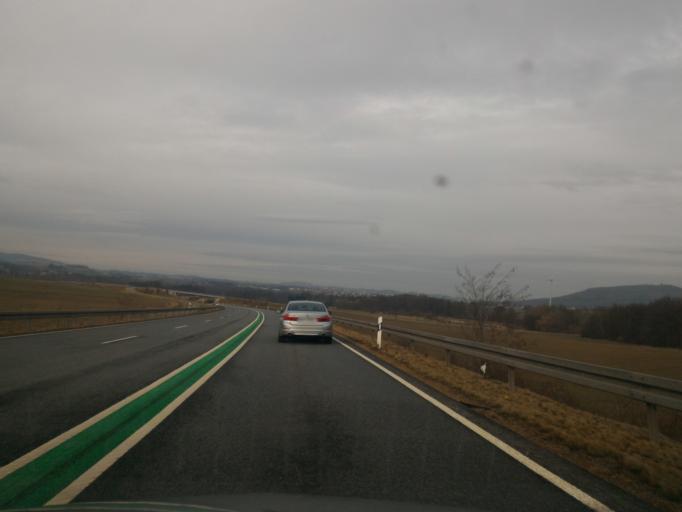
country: DE
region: Saxony
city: Niedercunnersdorf
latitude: 51.0578
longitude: 14.6743
